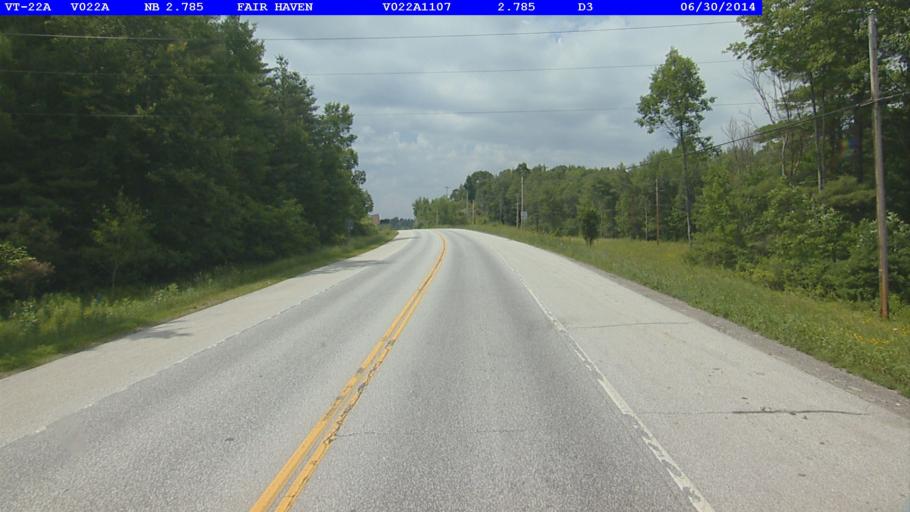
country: US
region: Vermont
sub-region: Rutland County
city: Fair Haven
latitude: 43.6086
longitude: -73.2810
